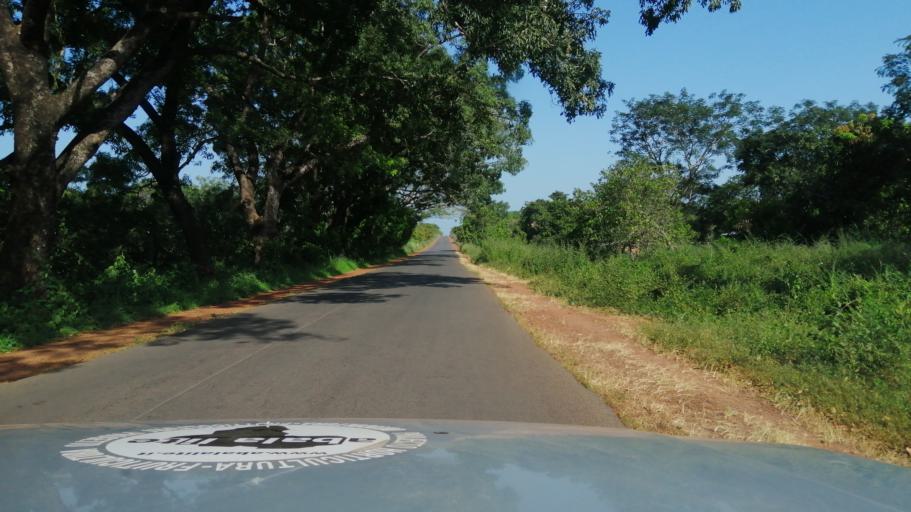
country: GW
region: Bissau
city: Bissau
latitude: 11.9588
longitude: -15.5291
